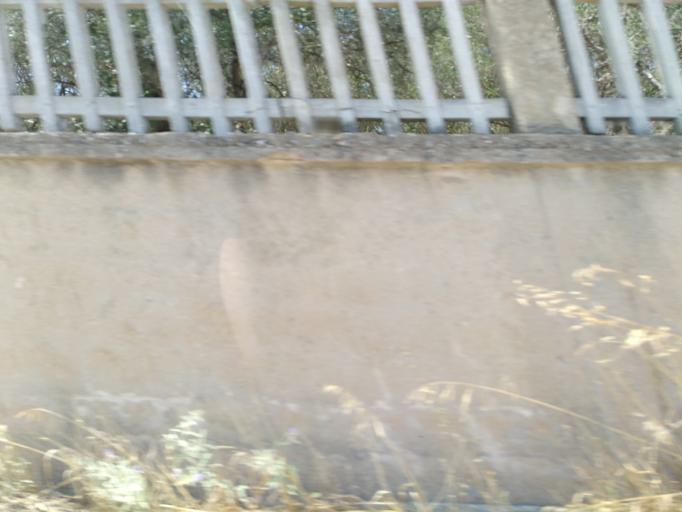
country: GR
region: Central Macedonia
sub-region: Nomos Thessalonikis
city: Agia Triada
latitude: 40.5025
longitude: 22.8462
